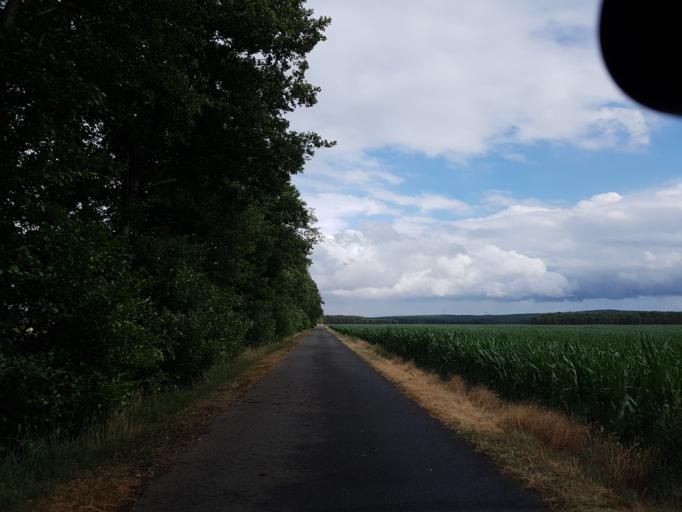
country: DE
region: Saxony-Anhalt
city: Jessen
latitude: 51.8341
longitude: 12.9515
